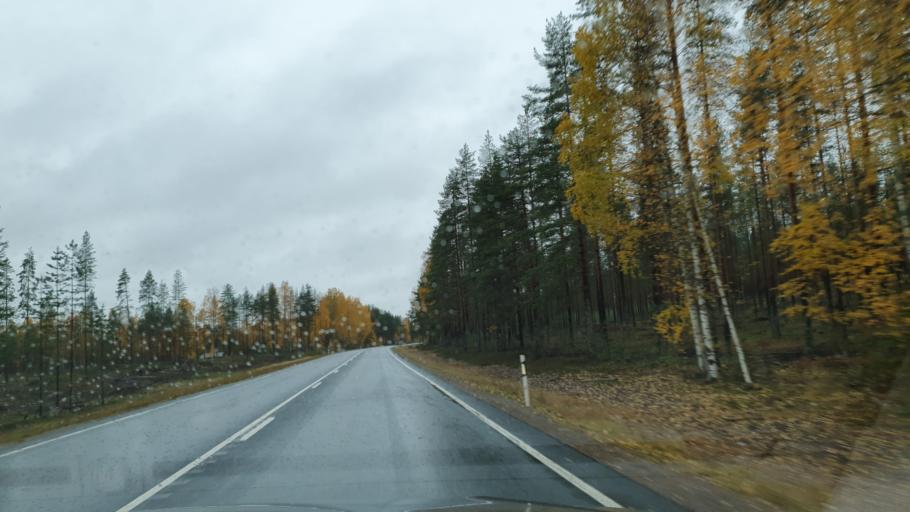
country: FI
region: Northern Ostrobothnia
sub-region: Oulunkaari
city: Pudasjaervi
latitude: 65.3966
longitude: 27.2541
